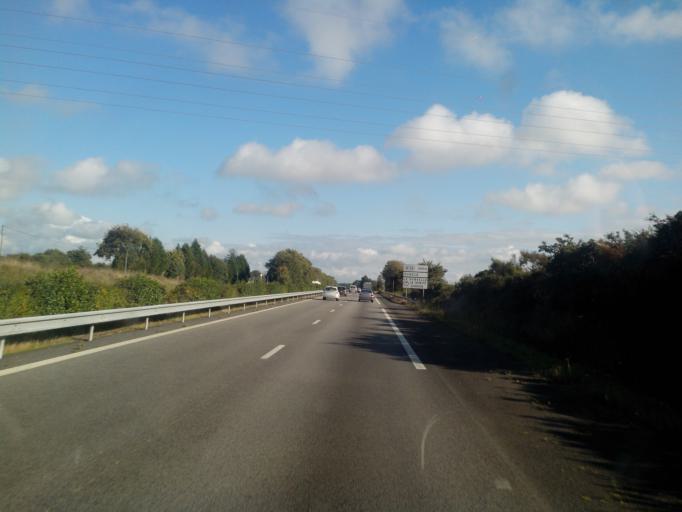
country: FR
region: Brittany
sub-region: Departement du Morbihan
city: Theix
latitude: 47.6199
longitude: -2.6272
